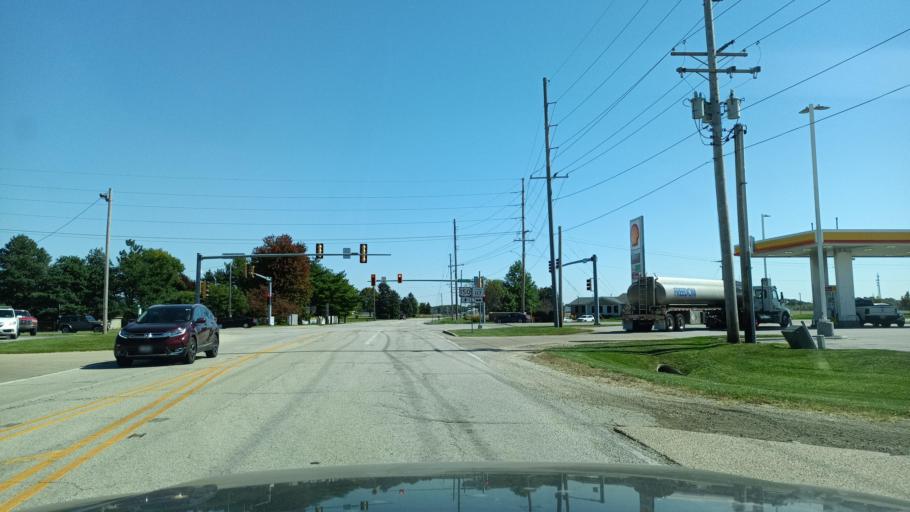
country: US
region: Illinois
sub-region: Woodford County
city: Eureka
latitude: 40.6277
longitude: -89.2759
